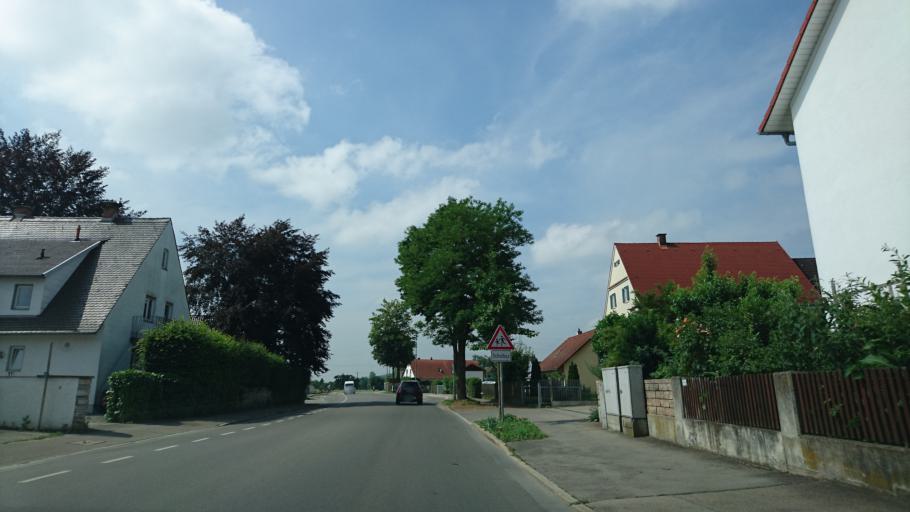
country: DE
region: Bavaria
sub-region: Swabia
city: Stadtbergen
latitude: 48.3630
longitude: 10.8442
